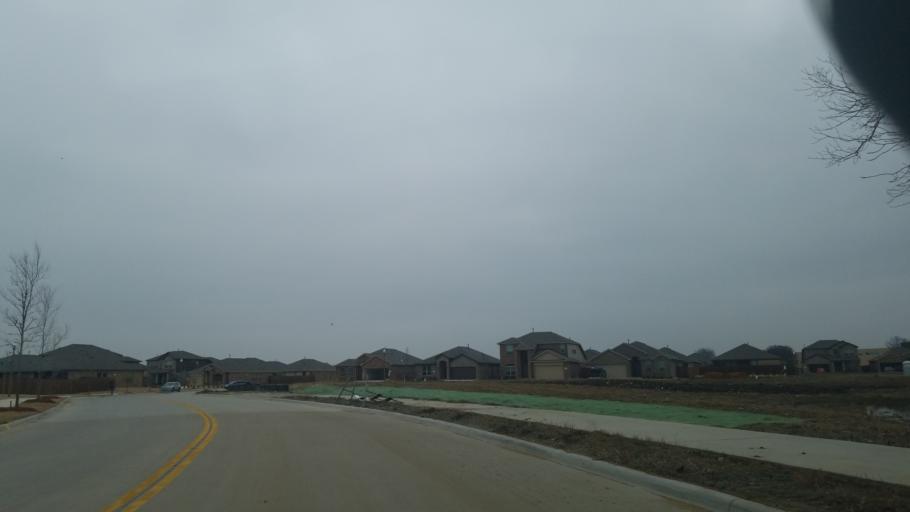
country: US
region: Texas
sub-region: Denton County
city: Denton
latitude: 33.1576
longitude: -97.1356
